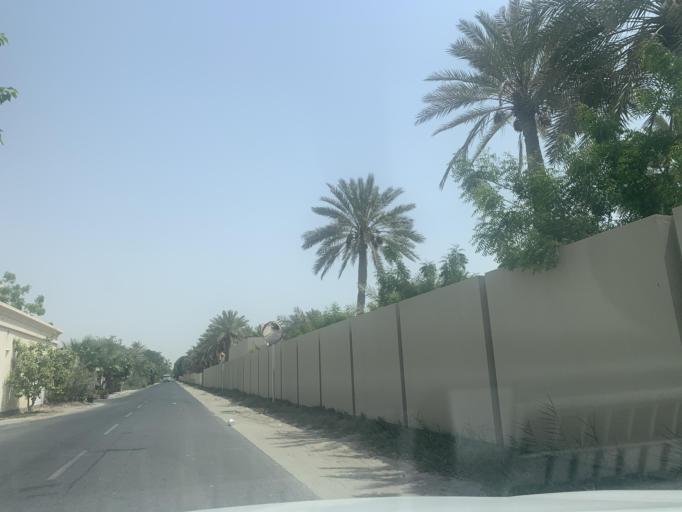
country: BH
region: Manama
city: Jidd Hafs
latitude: 26.2286
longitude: 50.4657
